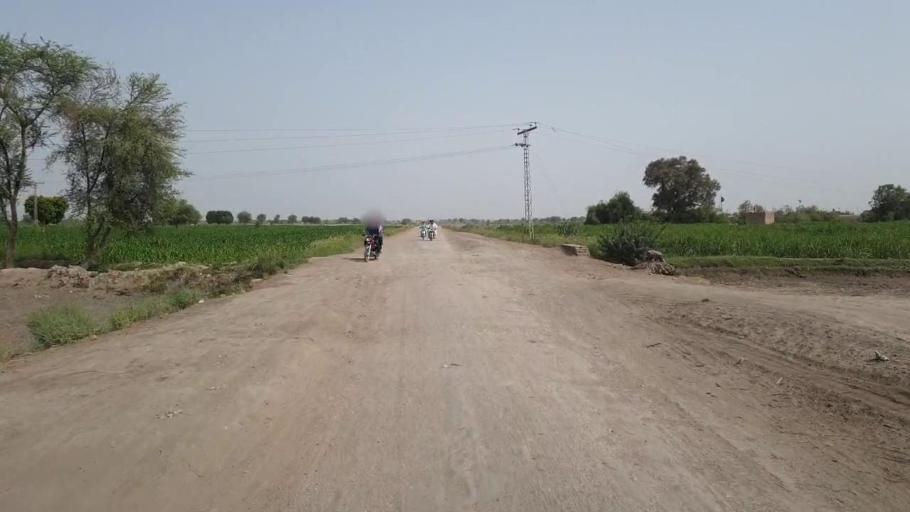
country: PK
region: Sindh
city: Daulatpur
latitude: 26.5543
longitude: 67.9905
